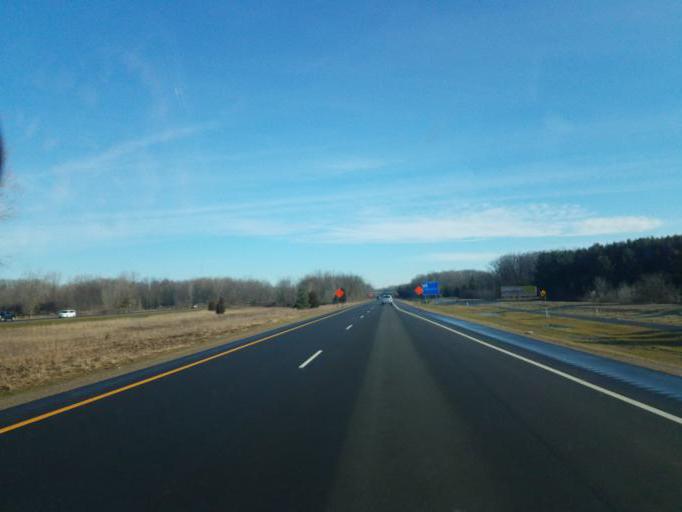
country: US
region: Michigan
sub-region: Gratiot County
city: Saint Louis
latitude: 43.3582
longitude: -84.6010
